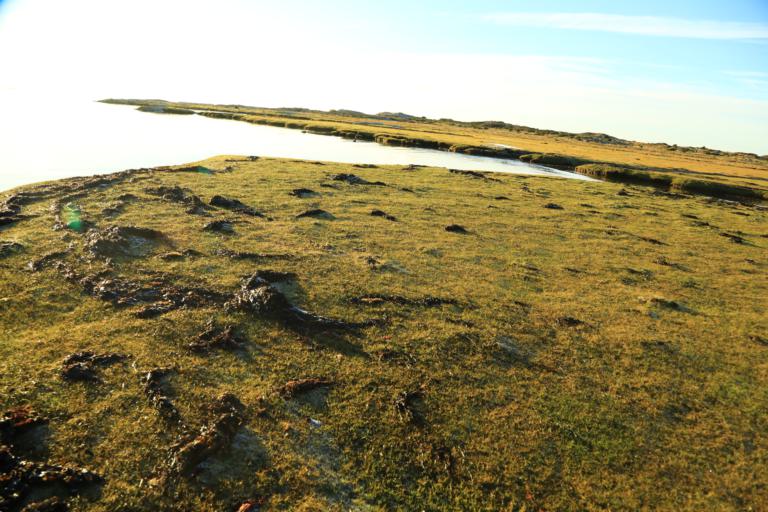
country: SE
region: Halland
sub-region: Kungsbacka Kommun
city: Frillesas
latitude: 57.1942
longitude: 12.1578
